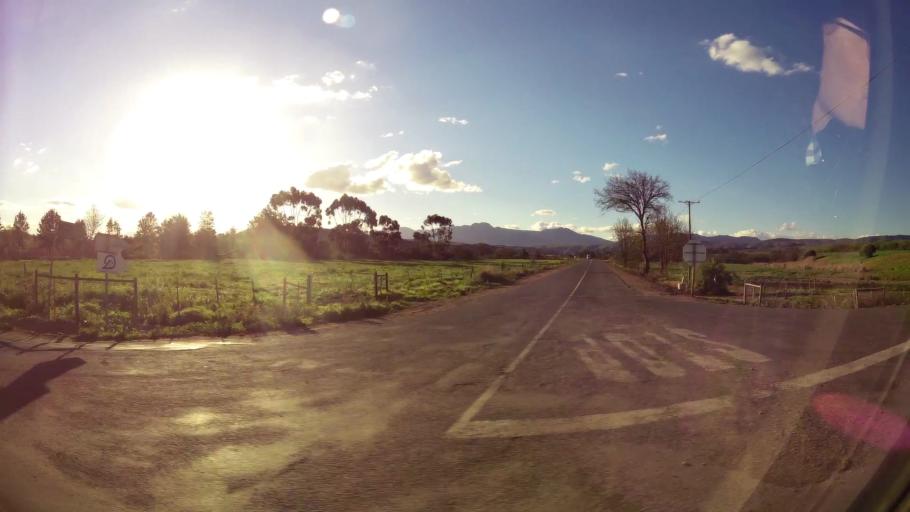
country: ZA
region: Western Cape
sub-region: Eden District Municipality
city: Riversdale
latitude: -34.0923
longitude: 20.9670
